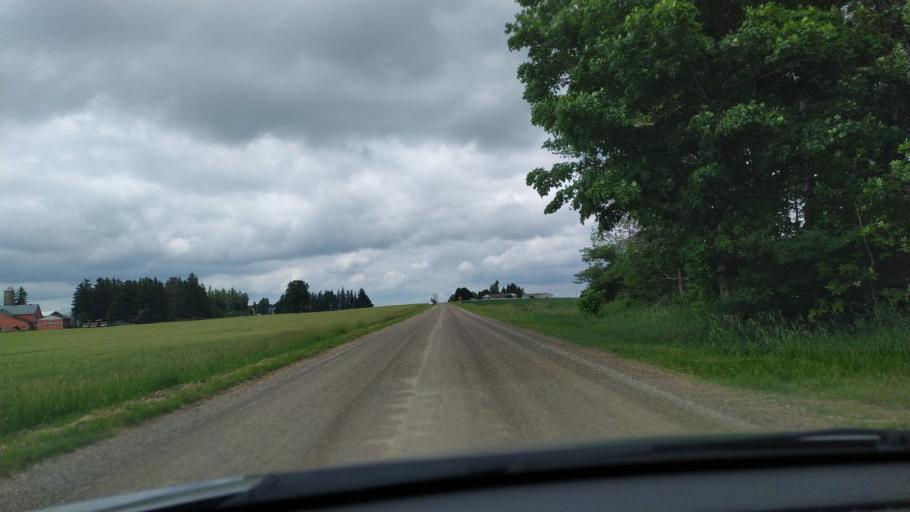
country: CA
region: Ontario
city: Stratford
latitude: 43.4202
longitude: -80.8883
